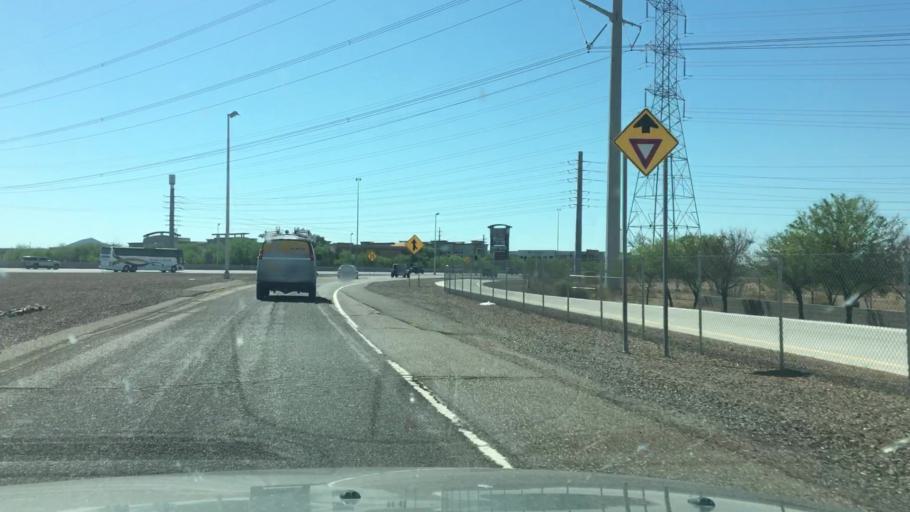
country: US
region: Arizona
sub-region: Maricopa County
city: Anthem
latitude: 33.7104
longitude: -112.1183
